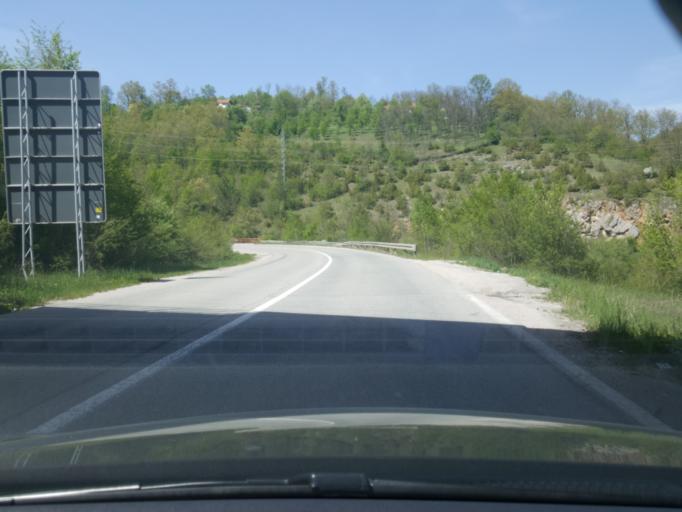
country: RS
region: Central Serbia
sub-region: Zlatiborski Okrug
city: Cajetina
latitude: 43.7860
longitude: 19.7349
